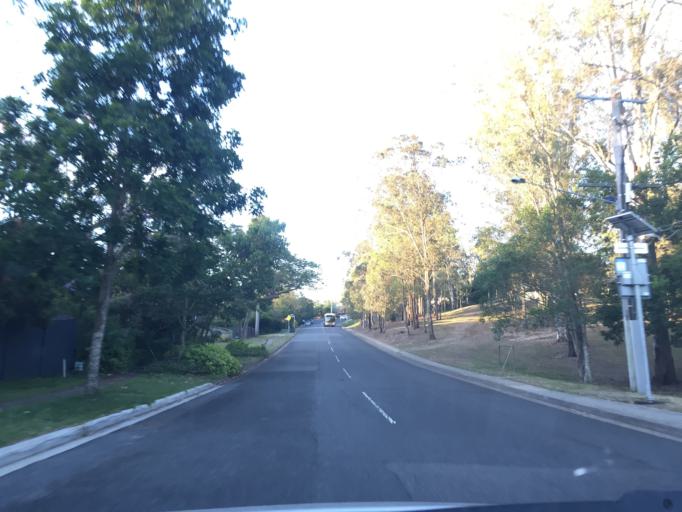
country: AU
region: Queensland
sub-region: Moreton Bay
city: Ferny Hills
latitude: -27.4445
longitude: 152.9400
